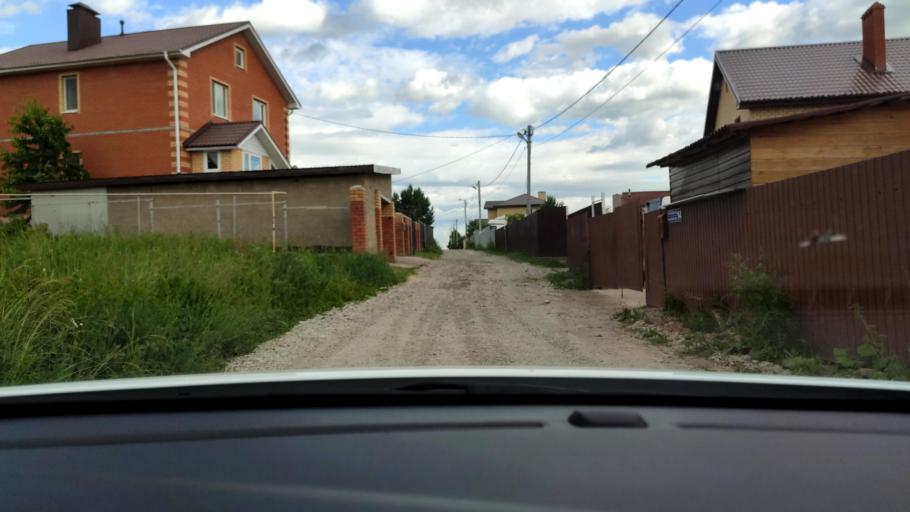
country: RU
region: Tatarstan
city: Stolbishchi
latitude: 55.7615
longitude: 49.3009
